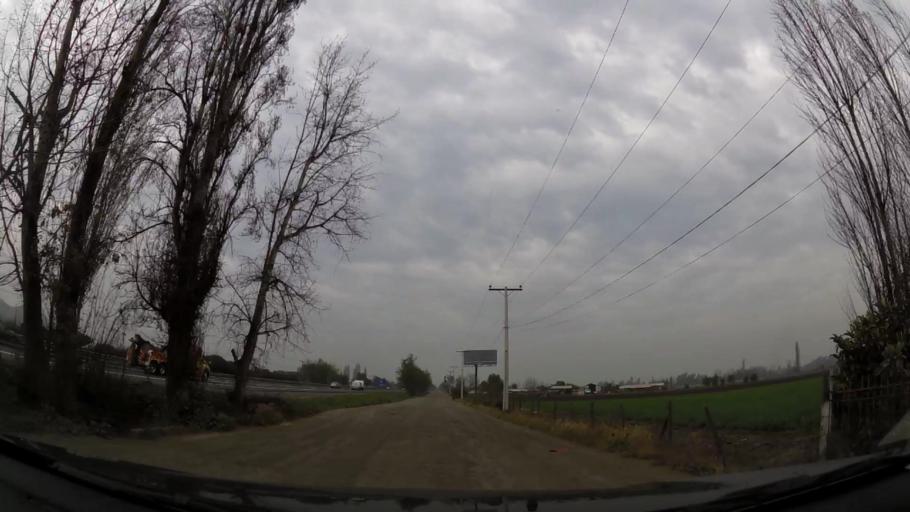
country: CL
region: Santiago Metropolitan
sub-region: Provincia de Chacabuco
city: Chicureo Abajo
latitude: -33.2253
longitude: -70.7638
